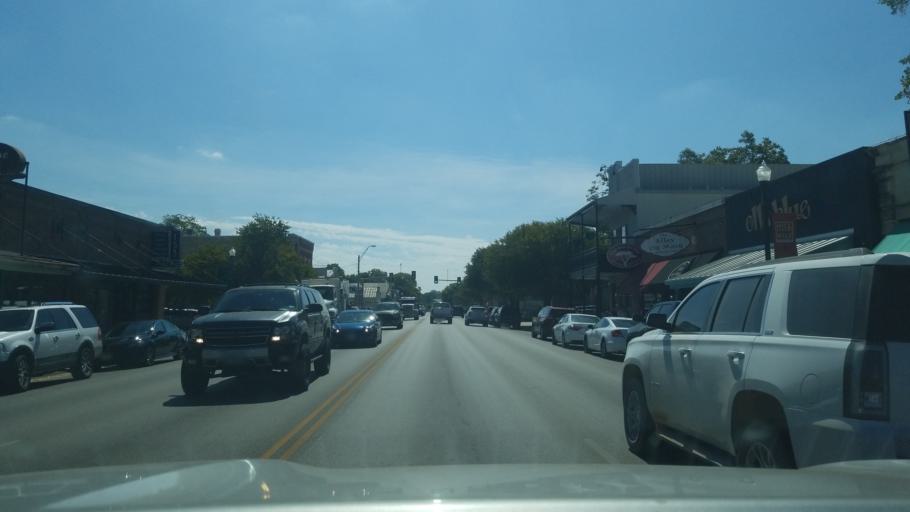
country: US
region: Texas
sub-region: Kendall County
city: Boerne
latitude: 29.7935
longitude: -98.7316
